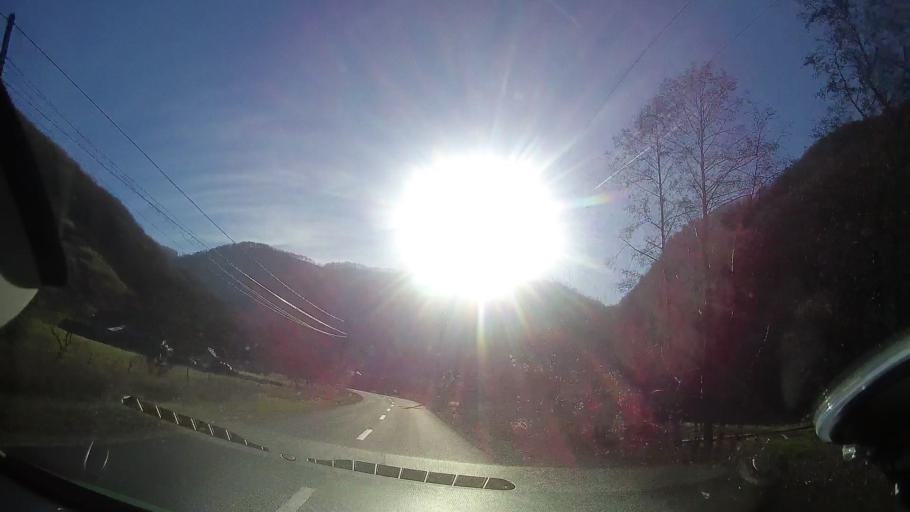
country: RO
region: Bihor
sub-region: Comuna Bulz
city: Bulz
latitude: 46.9201
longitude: 22.6543
